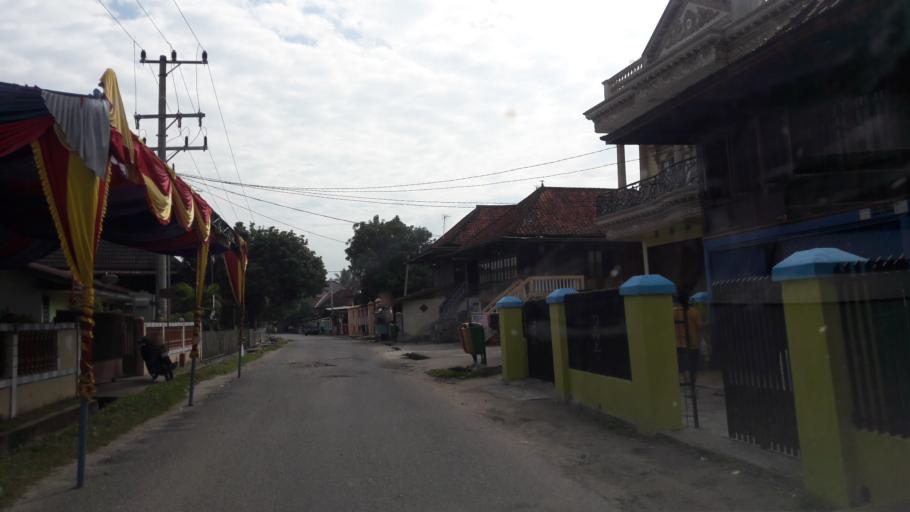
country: ID
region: South Sumatra
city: Gunungmenang
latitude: -3.0905
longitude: 104.0190
